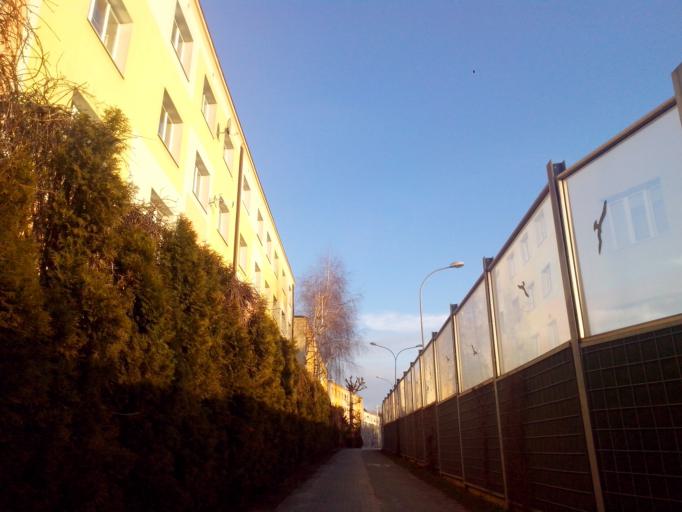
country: PL
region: Subcarpathian Voivodeship
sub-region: Rzeszow
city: Rzeszow
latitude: 50.0233
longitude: 21.9814
